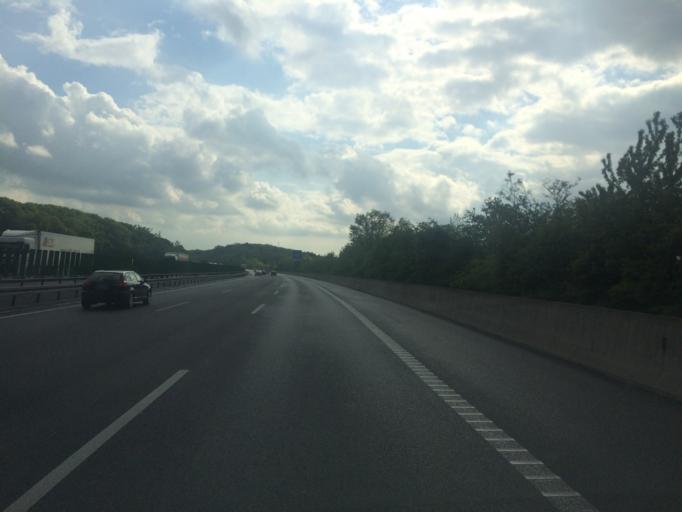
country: DE
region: Lower Saxony
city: Pohle
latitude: 52.2692
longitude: 9.3218
